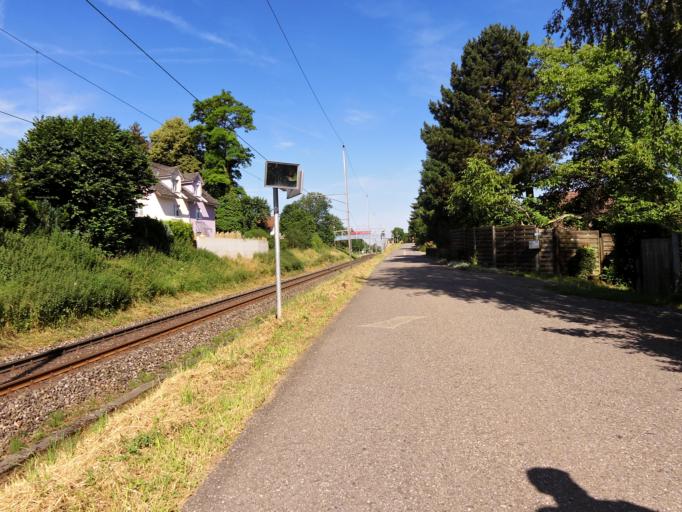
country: CH
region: Thurgau
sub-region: Kreuzlingen District
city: Munsterlingen
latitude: 47.6280
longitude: 9.2498
